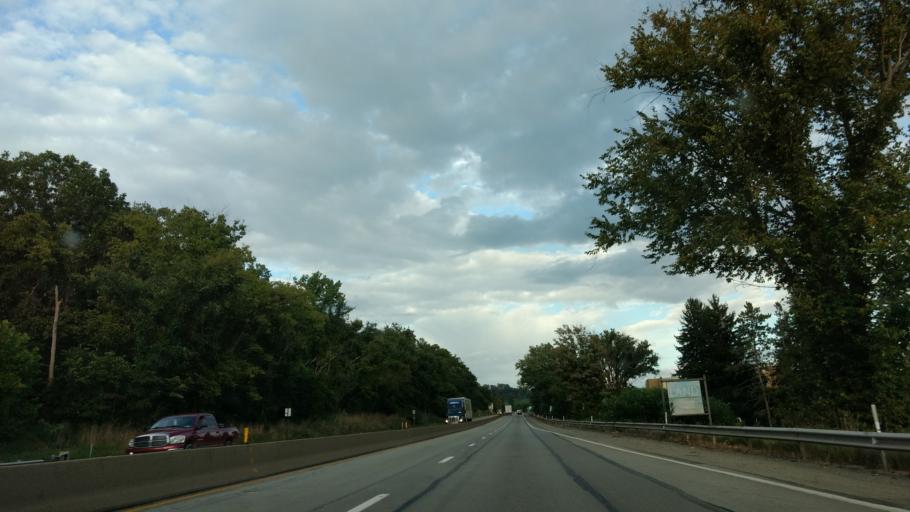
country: US
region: Pennsylvania
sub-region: Westmoreland County
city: Lynnwood-Pricedale
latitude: 40.1401
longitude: -79.8380
